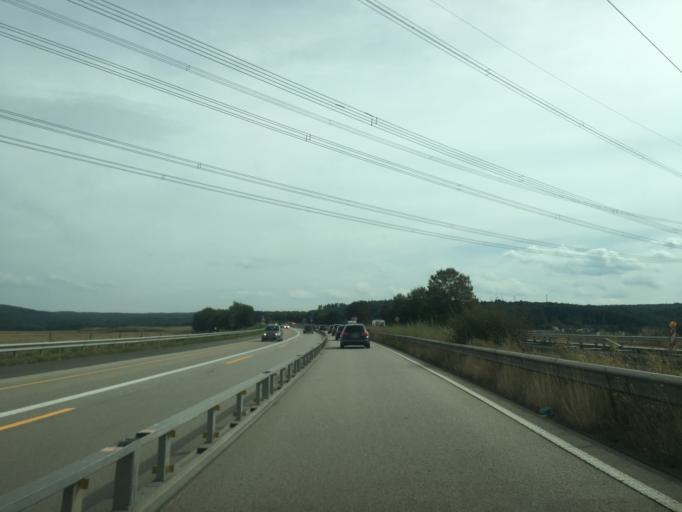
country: DE
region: Rheinland-Pfalz
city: Niederfell
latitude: 50.2999
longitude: 7.4911
